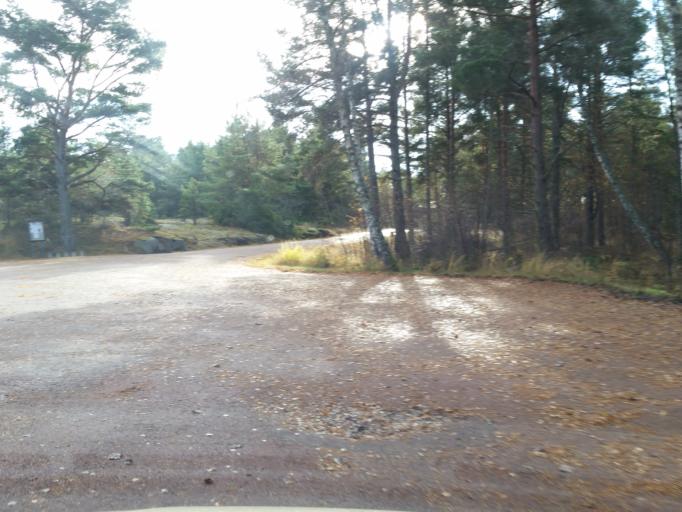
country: AX
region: Alands skaergard
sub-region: Kumlinge
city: Kumlinge
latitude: 60.2680
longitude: 20.7730
